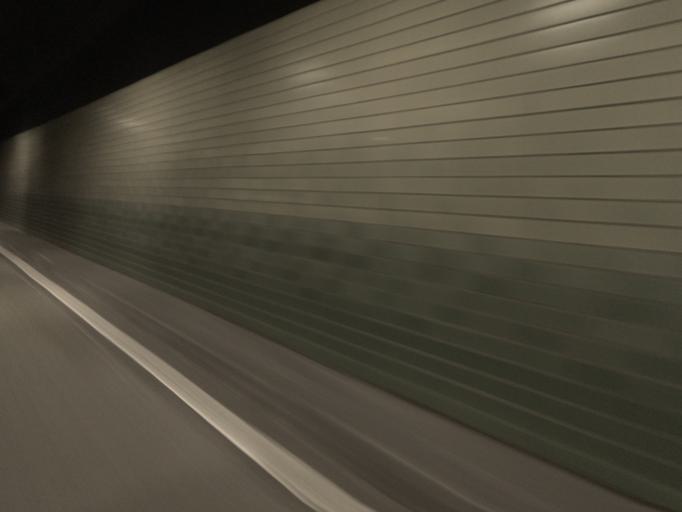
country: US
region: Hawaii
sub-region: Honolulu County
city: Kane'ohe
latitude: 21.3780
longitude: -157.8148
